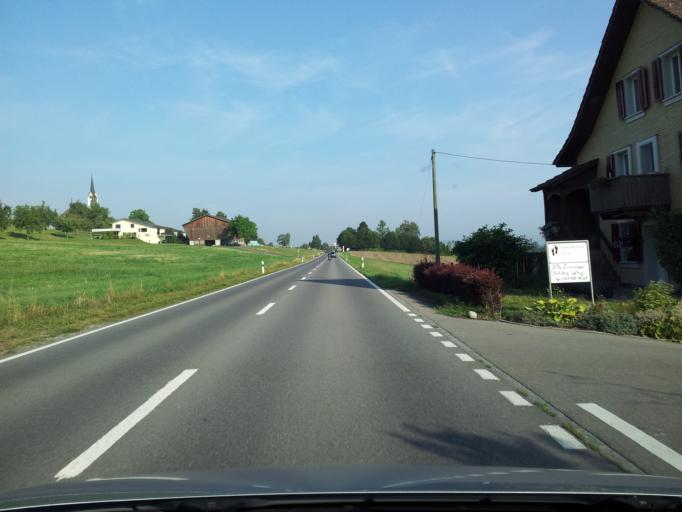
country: CH
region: Lucerne
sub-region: Sursee District
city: Nottwil
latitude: 47.1305
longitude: 8.1459
